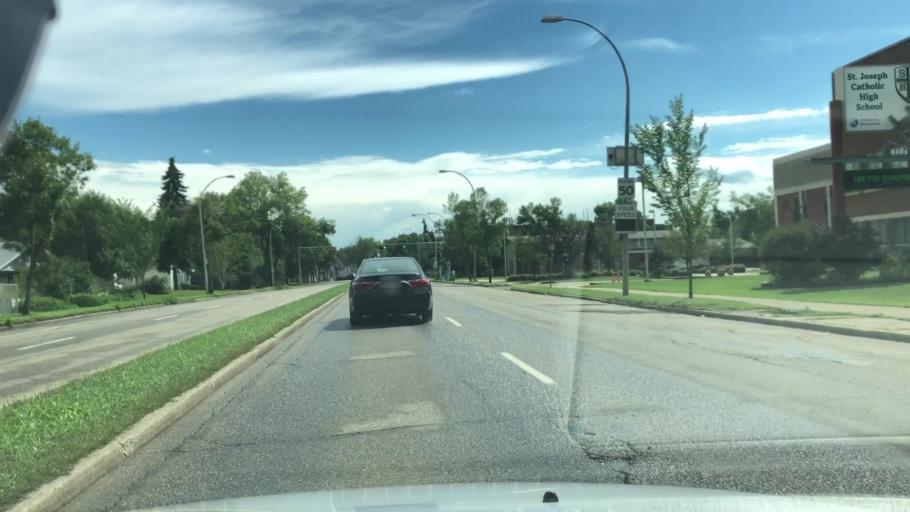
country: CA
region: Alberta
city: Edmonton
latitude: 53.5543
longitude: -113.5086
